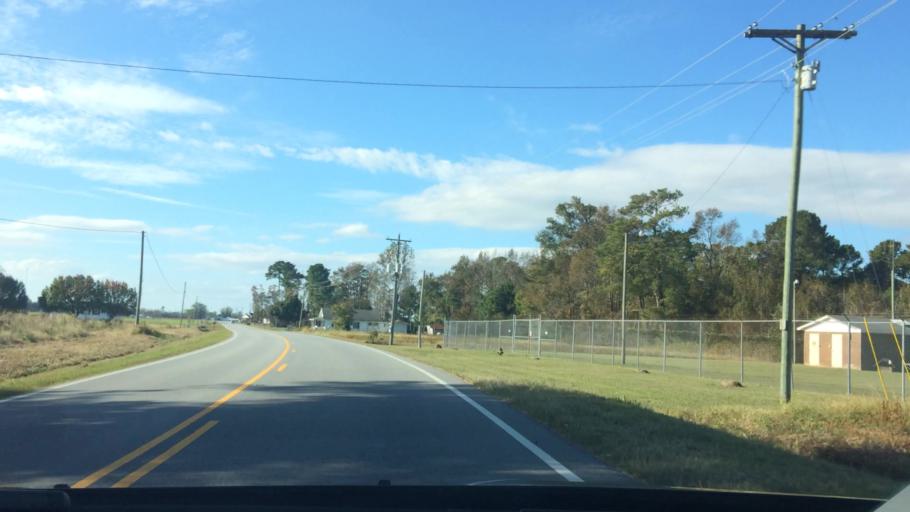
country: US
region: North Carolina
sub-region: Greene County
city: Maury
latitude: 35.4780
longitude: -77.6238
